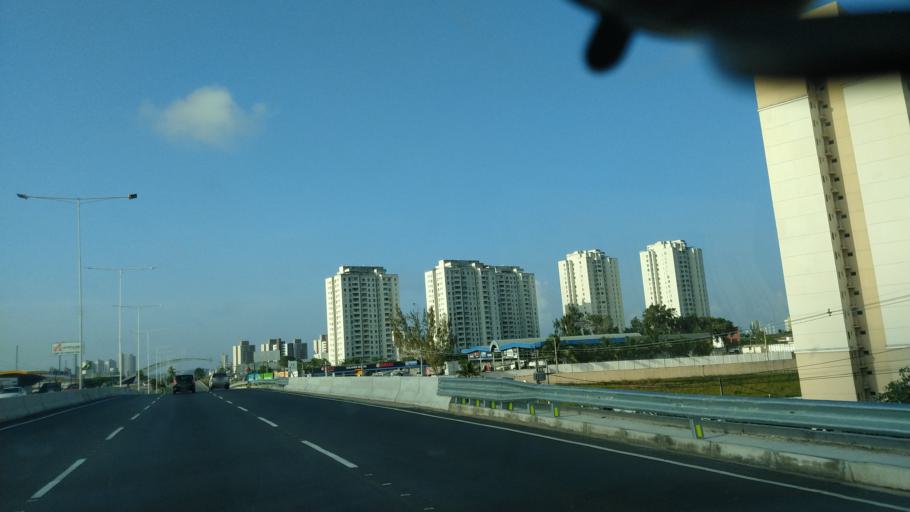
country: BR
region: Rio Grande do Norte
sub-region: Parnamirim
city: Parnamirim
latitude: -5.8697
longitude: -35.2185
